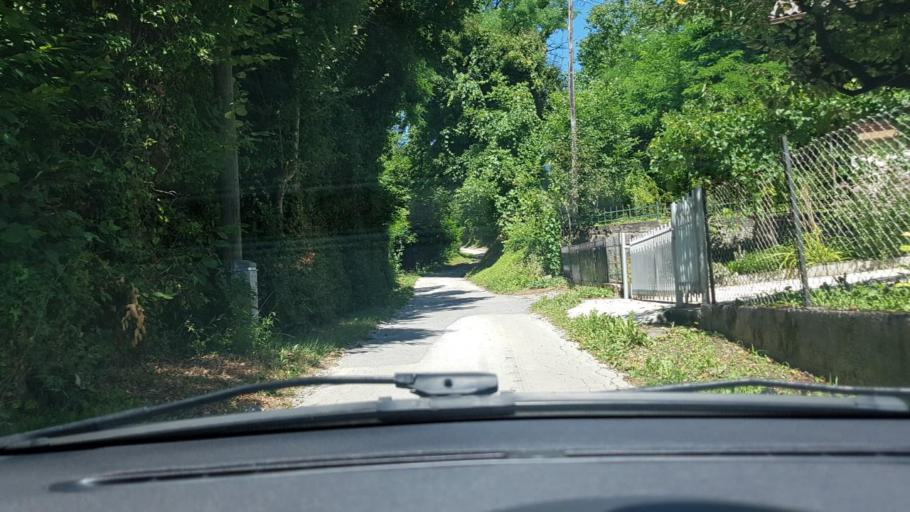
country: HR
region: Krapinsko-Zagorska
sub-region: Grad Krapina
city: Krapina
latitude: 46.1098
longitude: 15.8519
